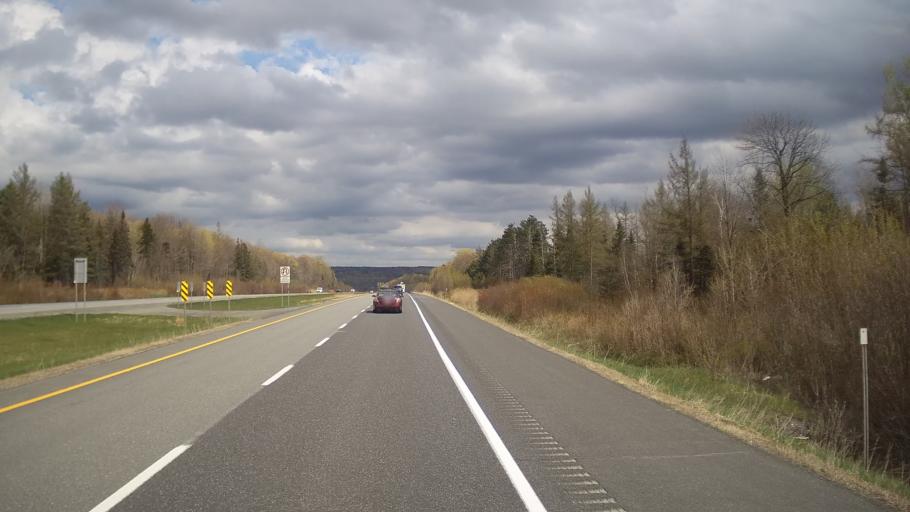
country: CA
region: Quebec
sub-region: Monteregie
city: Waterloo
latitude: 45.3034
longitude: -72.4707
